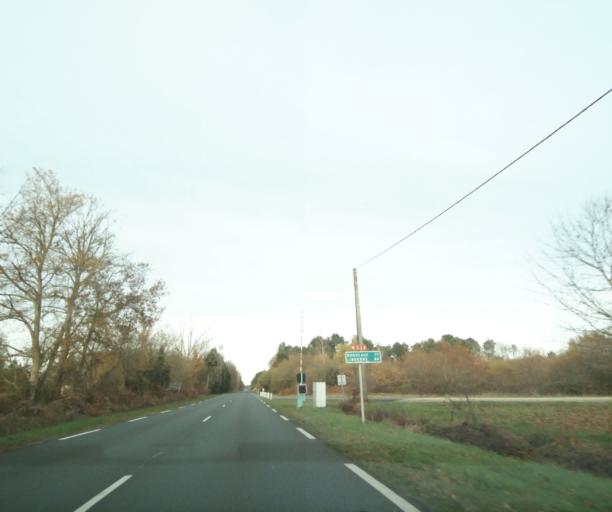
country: FR
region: Aquitaine
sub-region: Departement de la Gironde
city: Prechac
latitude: 44.2997
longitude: -0.2569
